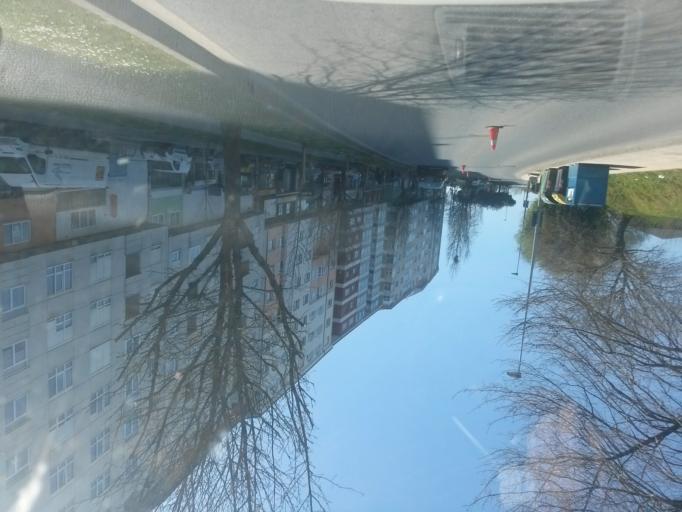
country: ES
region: Galicia
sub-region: Provincia de Lugo
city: Lugo
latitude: 43.0056
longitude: -7.5479
